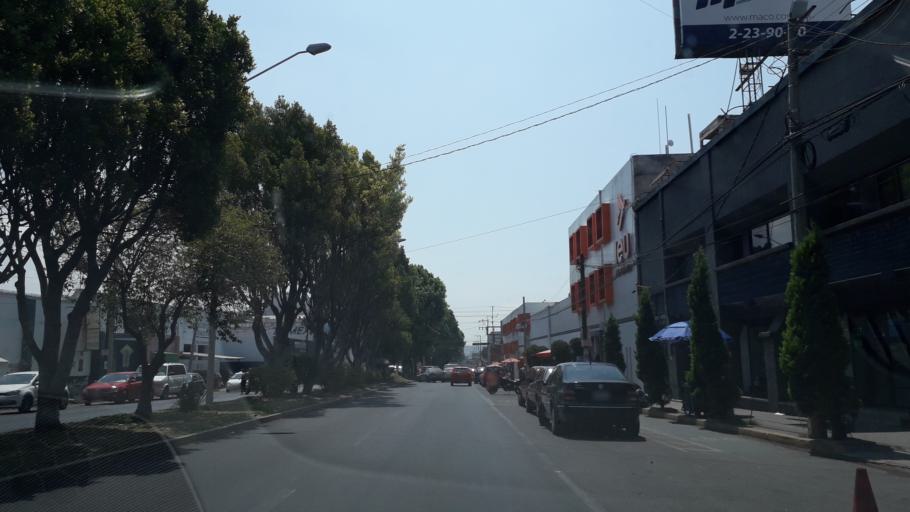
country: MX
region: Puebla
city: Puebla
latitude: 19.0535
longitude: -98.2123
